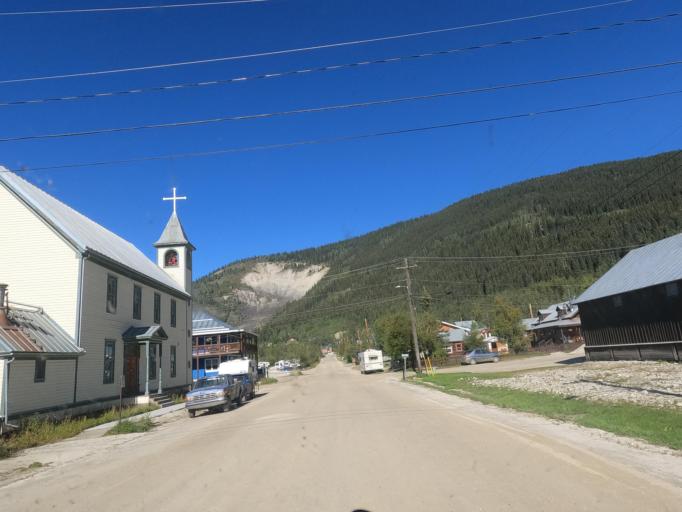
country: CA
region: Yukon
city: Dawson City
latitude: 64.0618
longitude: -139.4282
